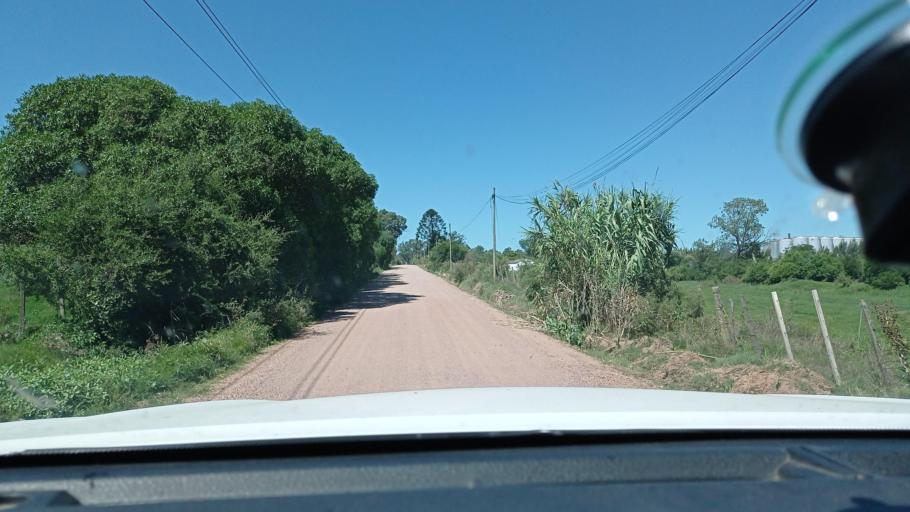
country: UY
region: Canelones
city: La Paz
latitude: -34.7602
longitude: -56.1764
